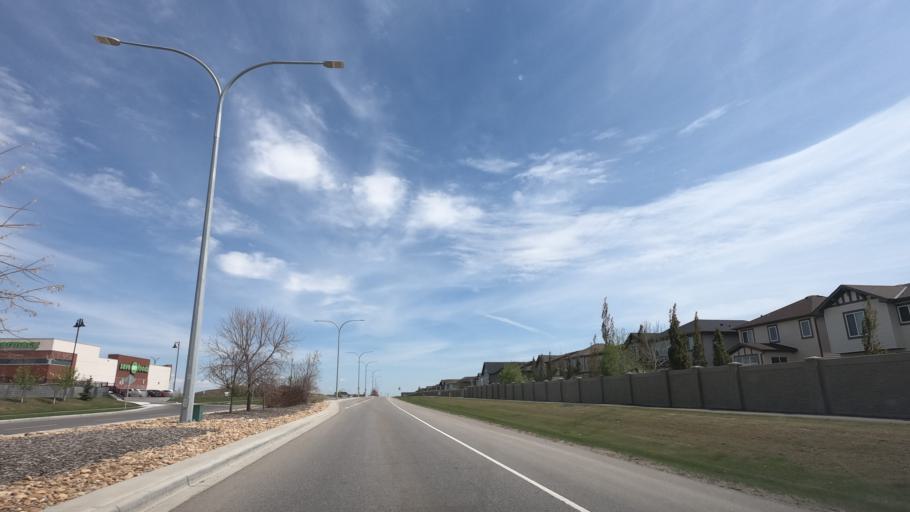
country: CA
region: Alberta
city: Airdrie
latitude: 51.2562
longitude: -114.0229
